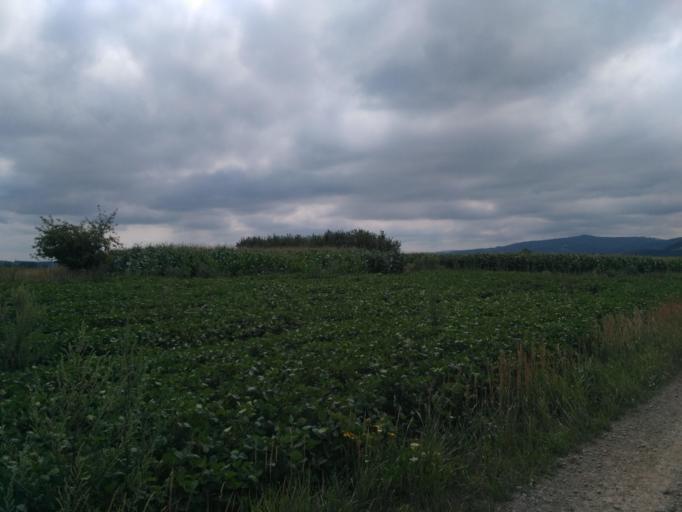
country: PL
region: Subcarpathian Voivodeship
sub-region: Powiat krosnienski
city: Rymanow
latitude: 49.5977
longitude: 21.8478
